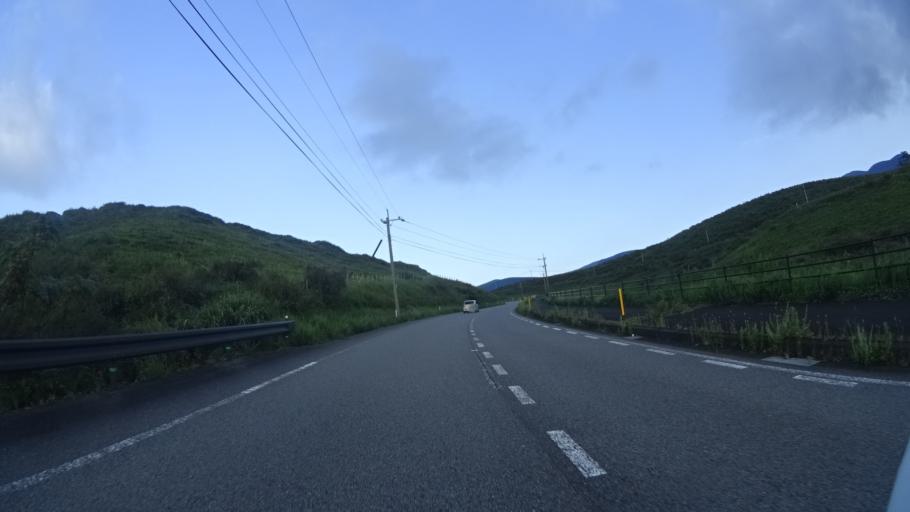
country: JP
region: Oita
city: Beppu
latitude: 33.3425
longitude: 131.4173
